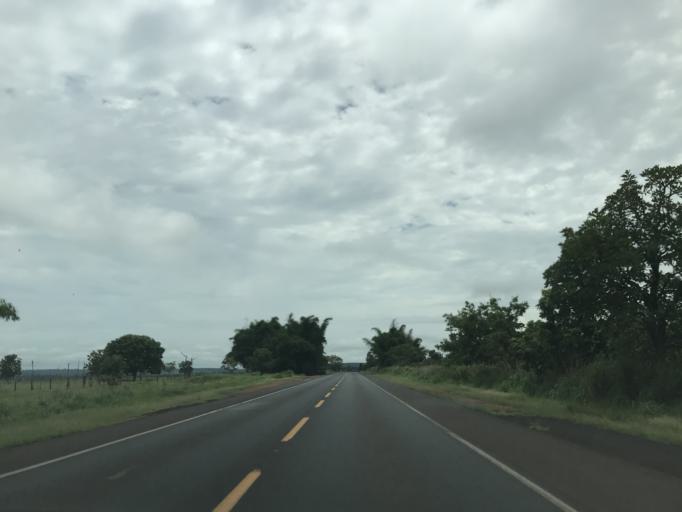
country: BR
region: Minas Gerais
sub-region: Frutal
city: Frutal
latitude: -19.9473
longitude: -48.9676
